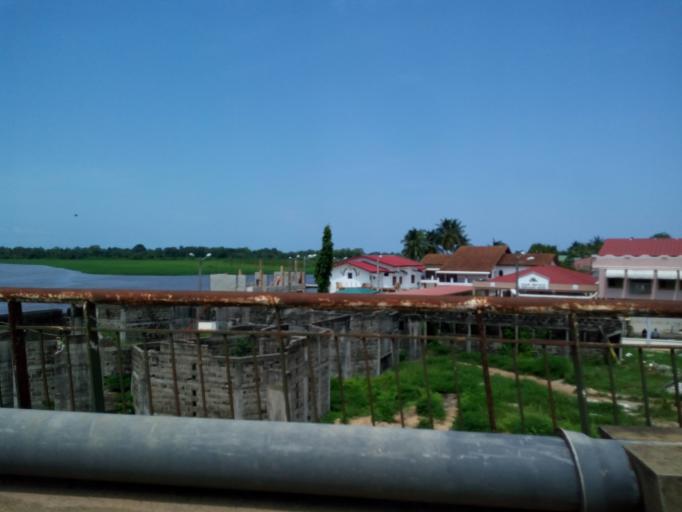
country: CI
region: Sud-Comoe
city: Grand-Bassam
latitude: 5.2208
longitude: -3.7229
